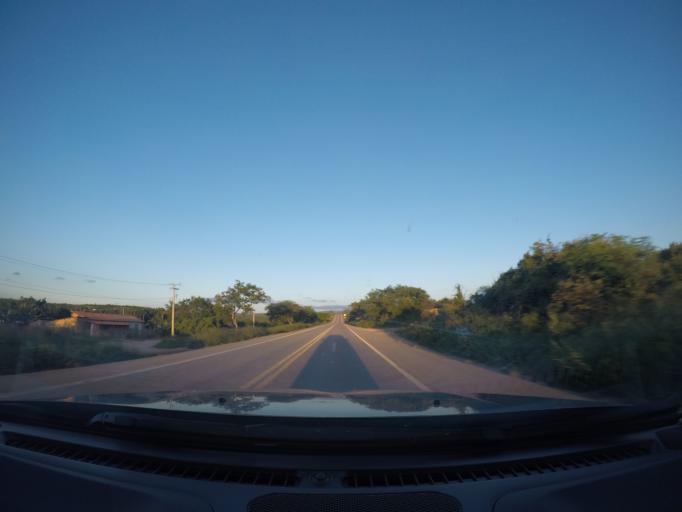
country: BR
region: Bahia
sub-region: Seabra
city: Seabra
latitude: -12.3968
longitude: -41.9343
